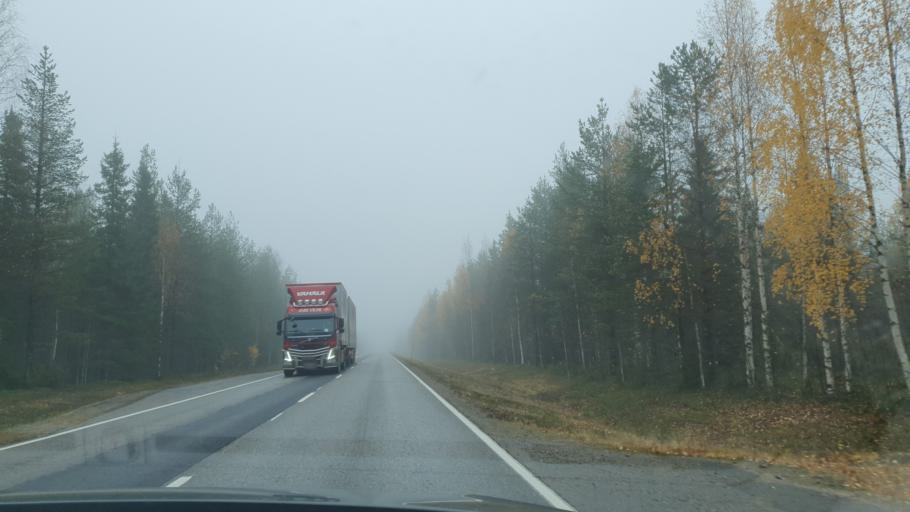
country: FI
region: Lapland
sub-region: Tunturi-Lappi
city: Kittilae
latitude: 67.2463
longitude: 24.9126
